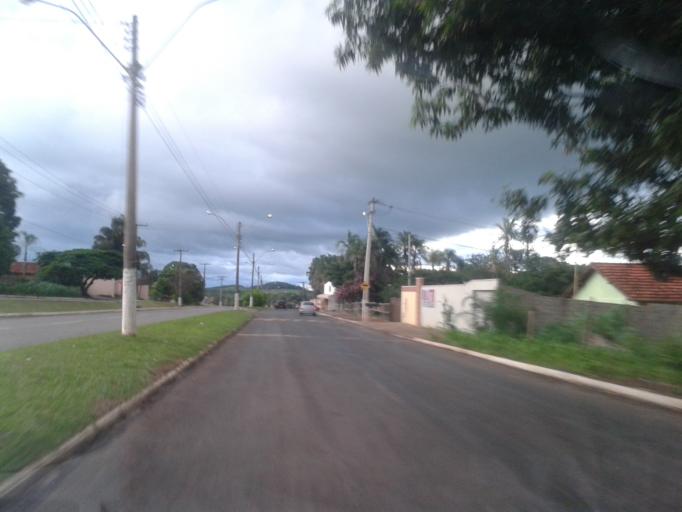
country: BR
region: Goias
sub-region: Morrinhos
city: Morrinhos
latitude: -17.7306
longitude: -49.1484
